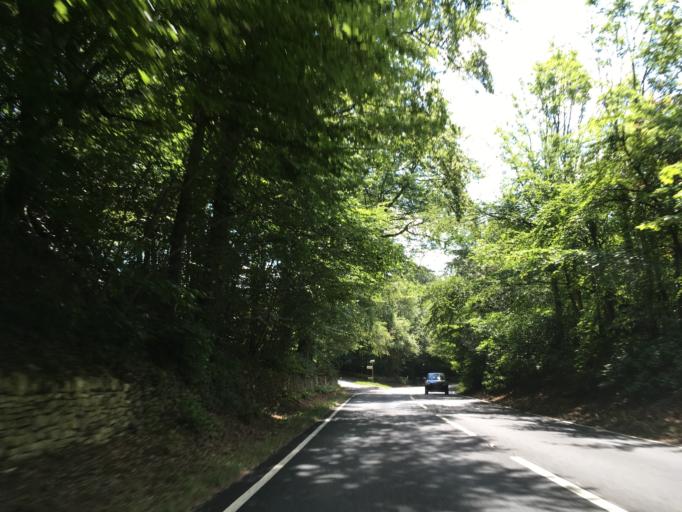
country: GB
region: England
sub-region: Gloucestershire
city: Painswick
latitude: 51.7973
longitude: -2.1960
